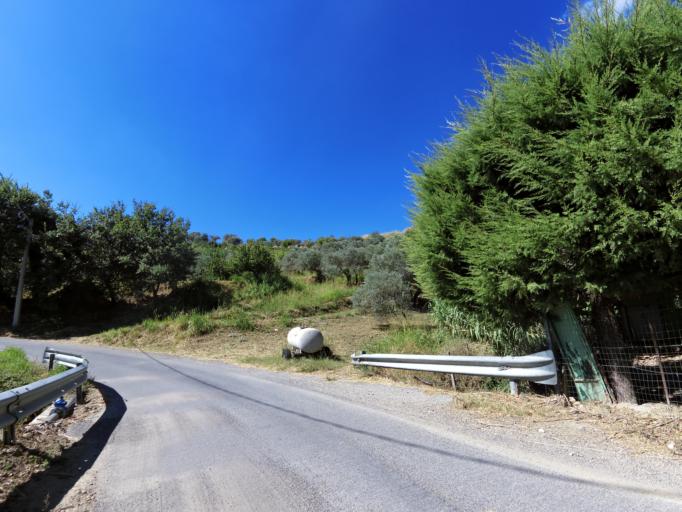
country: IT
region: Calabria
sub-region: Provincia di Reggio Calabria
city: Pazzano
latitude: 38.4633
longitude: 16.4521
